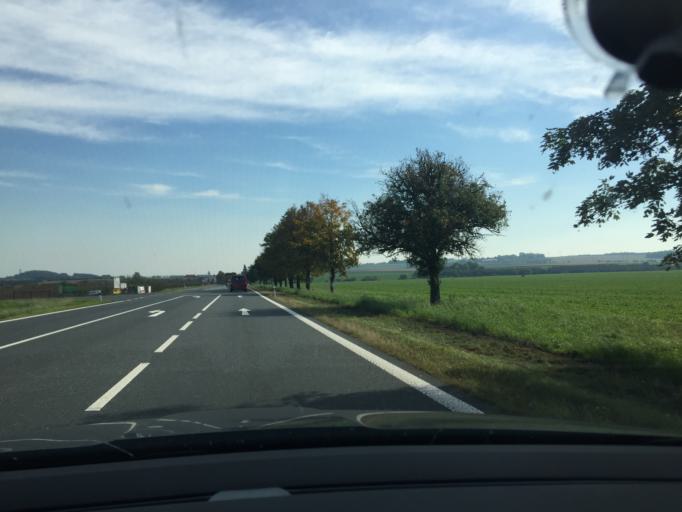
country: CZ
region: Central Bohemia
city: Velim
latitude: 50.0431
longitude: 15.0865
